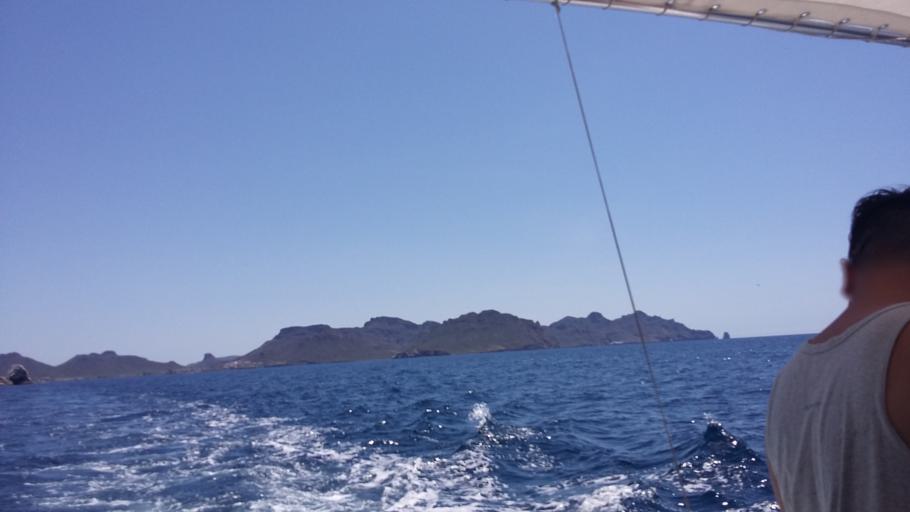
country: MX
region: Sonora
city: Heroica Guaymas
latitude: 27.9267
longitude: -111.0033
